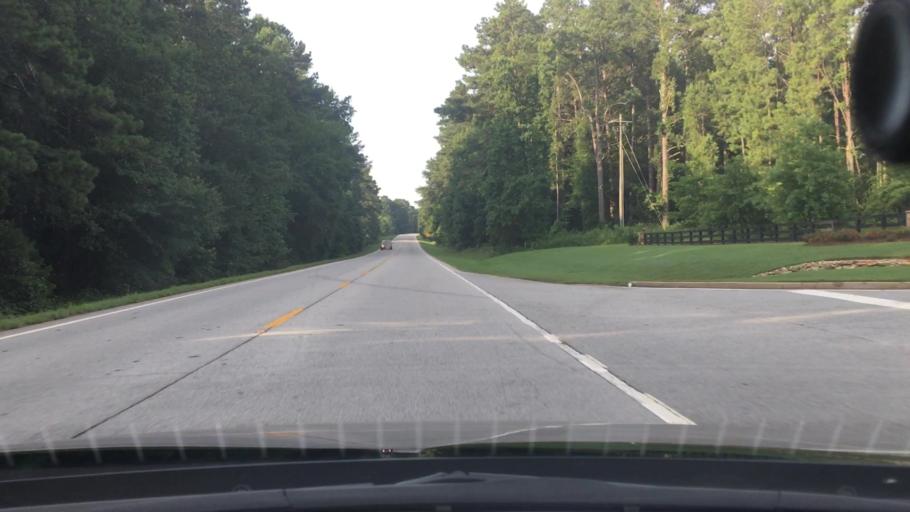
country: US
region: Georgia
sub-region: Fayette County
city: Peachtree City
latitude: 33.3712
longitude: -84.6282
